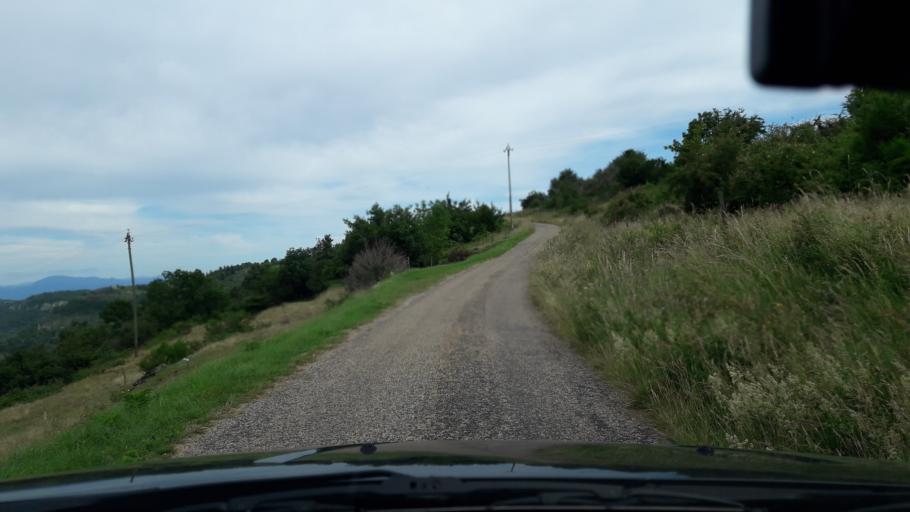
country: FR
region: Rhone-Alpes
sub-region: Departement de l'Ardeche
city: Saint-Priest
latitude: 44.6824
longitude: 4.5691
